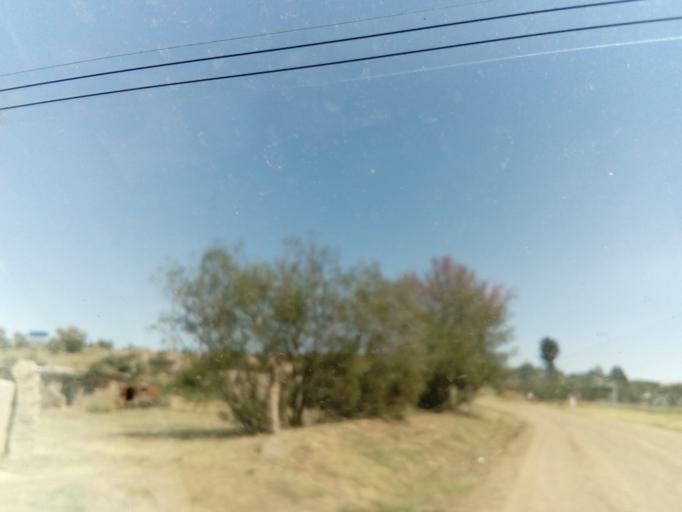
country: LS
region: Berea
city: Teyateyaneng
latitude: -29.1409
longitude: 27.8812
